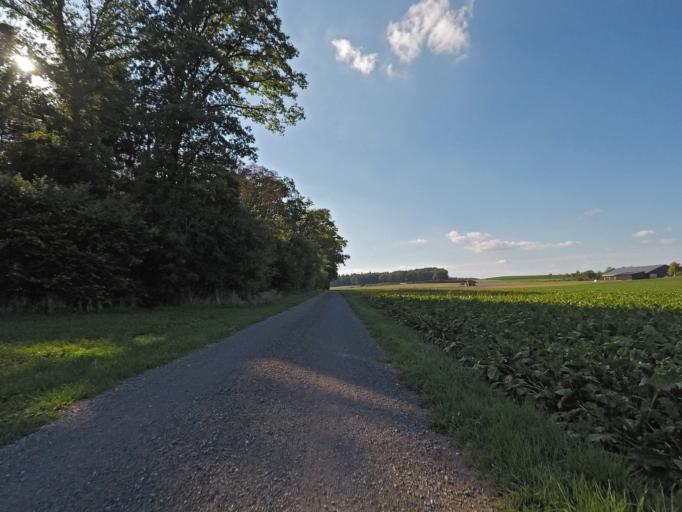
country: CH
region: Thurgau
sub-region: Frauenfeld District
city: Diessenhofen
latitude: 47.6598
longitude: 8.7422
